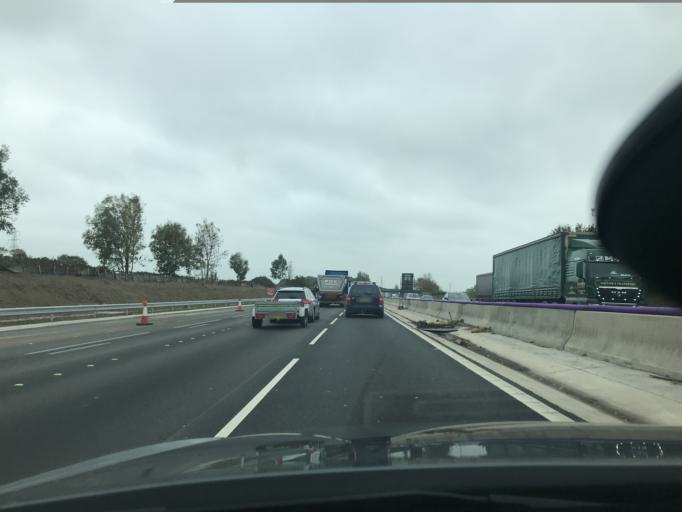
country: GB
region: England
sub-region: Cheshire East
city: Knutsford
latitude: 53.2912
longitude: -2.3962
